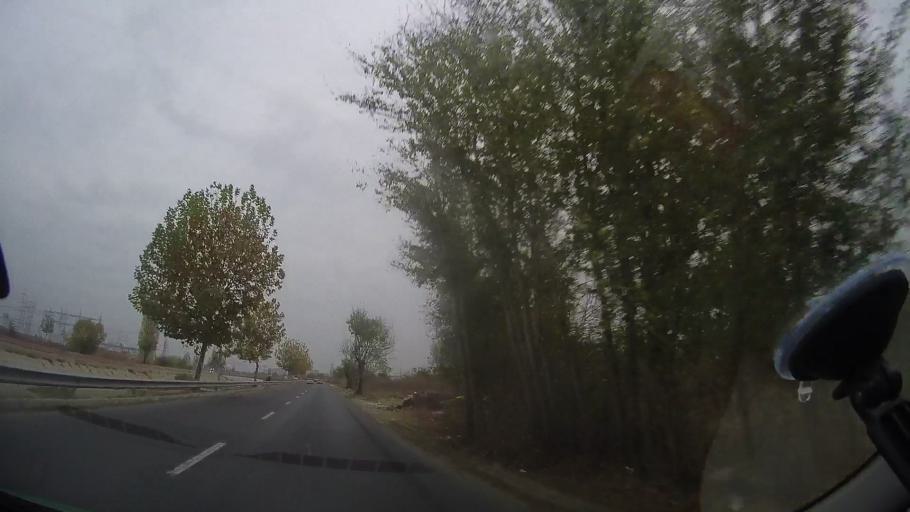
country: RO
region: Ilfov
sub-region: Comuna Popesti-Leordeni
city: Popesti-Leordeni
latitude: 44.3947
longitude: 26.1764
